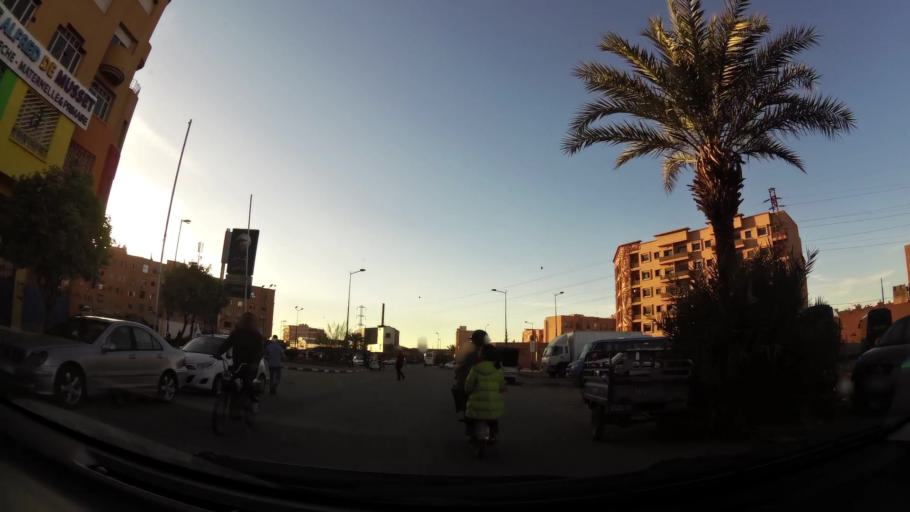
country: MA
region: Marrakech-Tensift-Al Haouz
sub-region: Marrakech
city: Marrakesh
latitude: 31.6234
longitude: -8.0291
